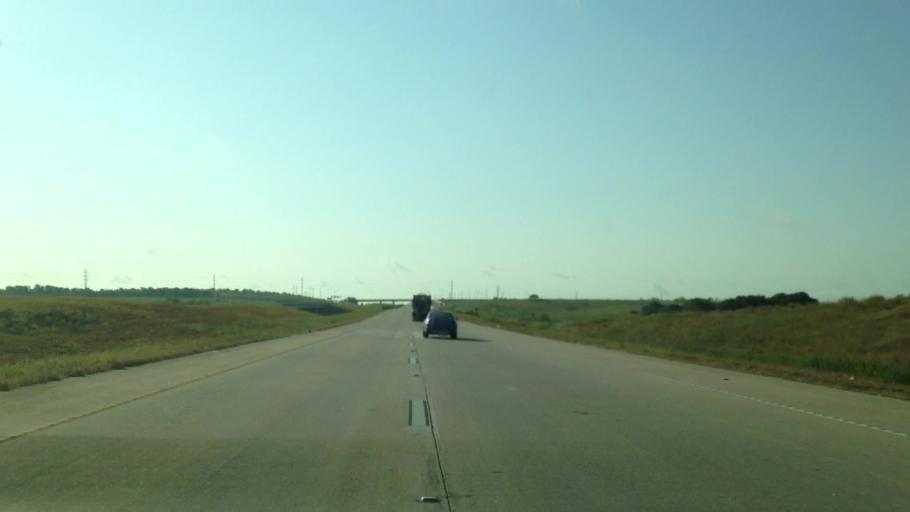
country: US
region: Texas
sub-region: Travis County
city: Onion Creek
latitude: 30.1092
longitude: -97.7936
